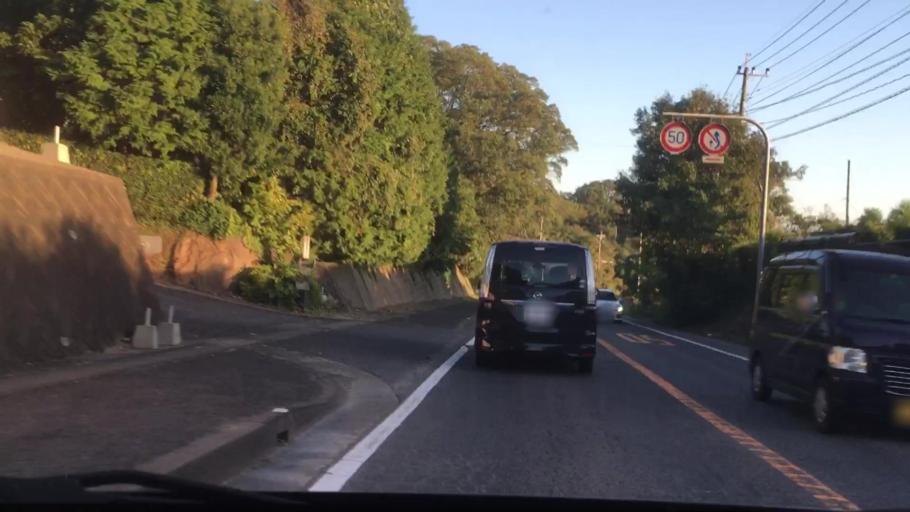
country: JP
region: Nagasaki
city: Sasebo
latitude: 33.0695
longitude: 129.7629
